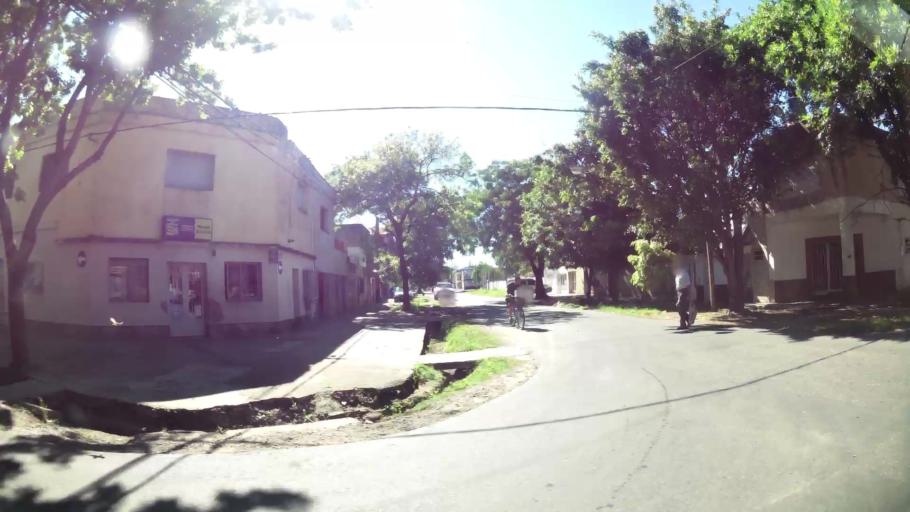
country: AR
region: Santa Fe
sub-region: Departamento de Rosario
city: Rosario
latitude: -32.9554
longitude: -60.6846
